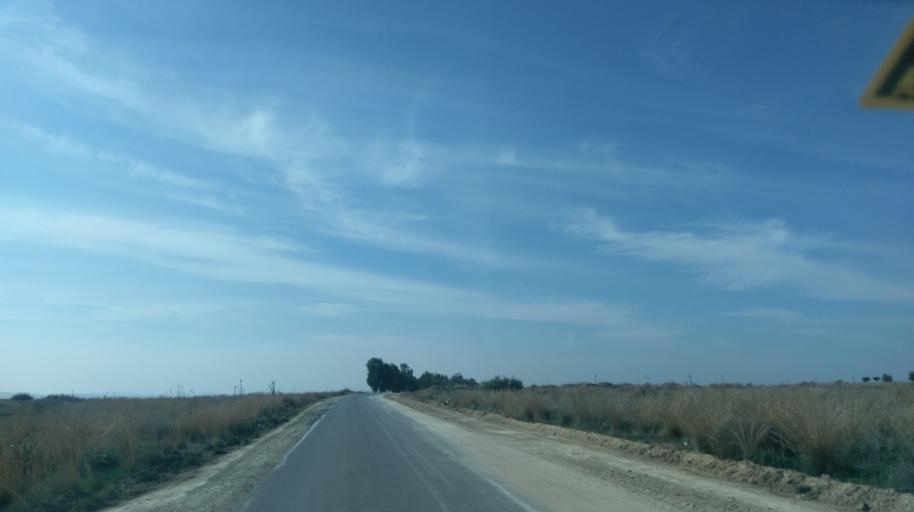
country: CY
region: Larnaka
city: Pergamos
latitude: 35.1489
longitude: 33.6792
